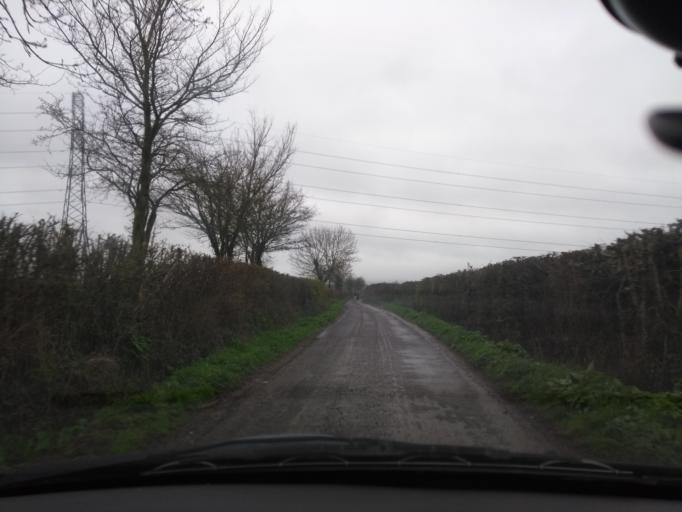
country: GB
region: England
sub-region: Somerset
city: Taunton
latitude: 51.0413
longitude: -3.1201
